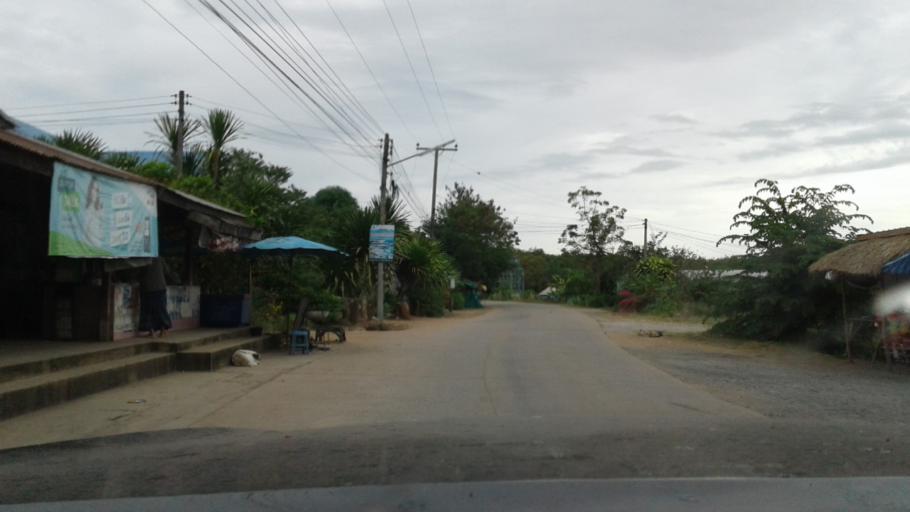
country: TH
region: Changwat Udon Thani
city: Nong Wua So
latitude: 17.2358
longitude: 102.5330
